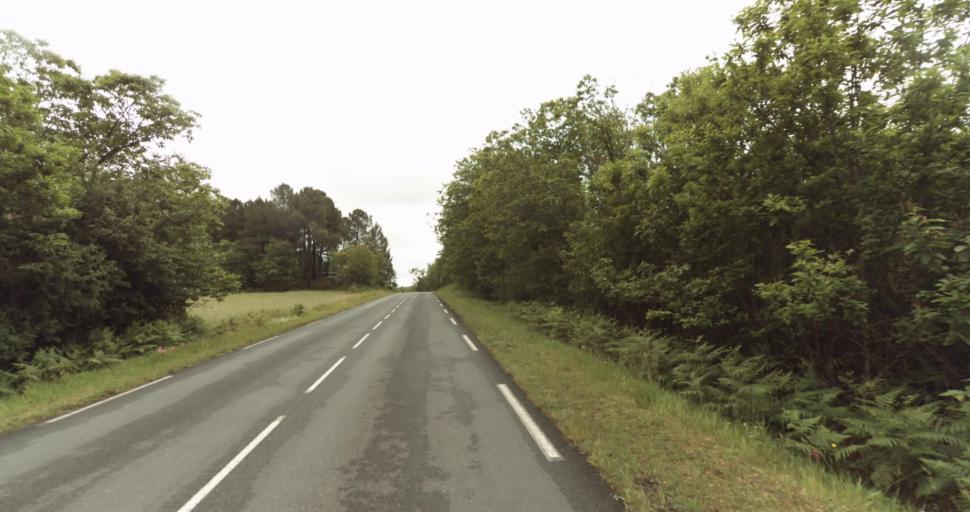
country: FR
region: Aquitaine
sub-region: Departement de la Dordogne
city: Belves
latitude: 44.6723
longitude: 0.9985
